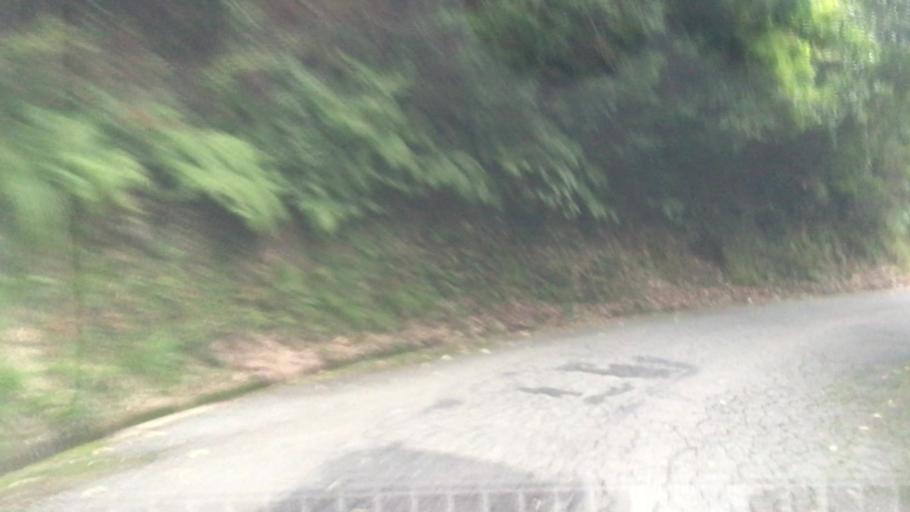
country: JP
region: Hyogo
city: Toyooka
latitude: 35.6215
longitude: 134.8767
